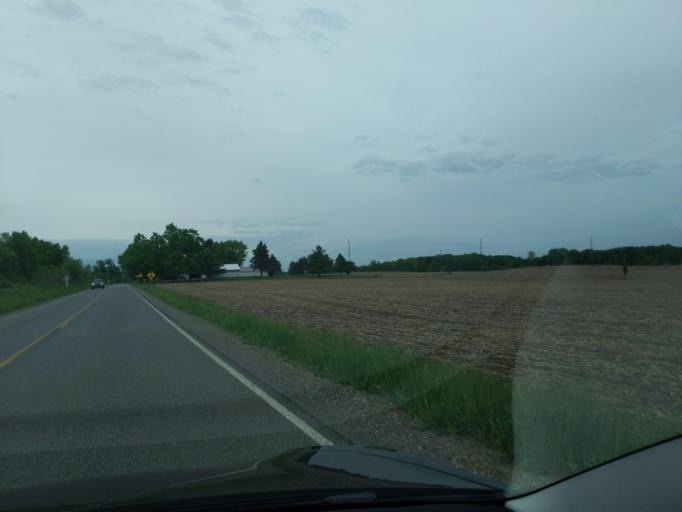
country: US
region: Michigan
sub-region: Ingham County
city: Leslie
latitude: 42.5103
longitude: -84.4281
